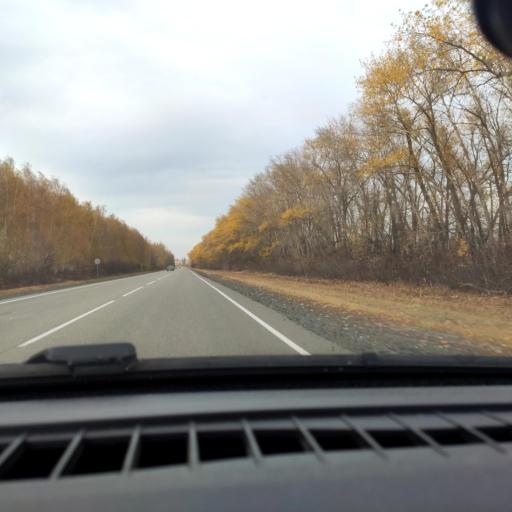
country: RU
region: Voronezj
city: Ostrogozhsk
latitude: 50.9936
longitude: 38.9988
